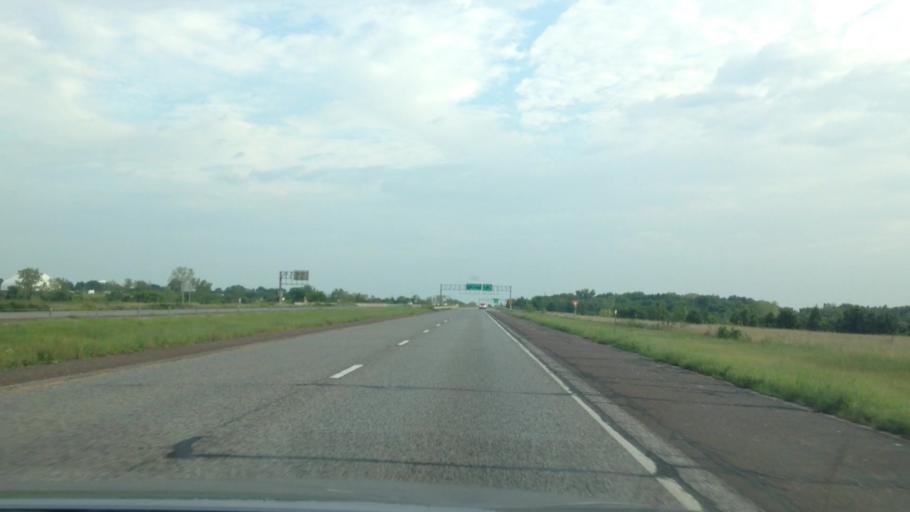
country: US
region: Missouri
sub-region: Clay County
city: Smithville
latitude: 39.3126
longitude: -94.5846
